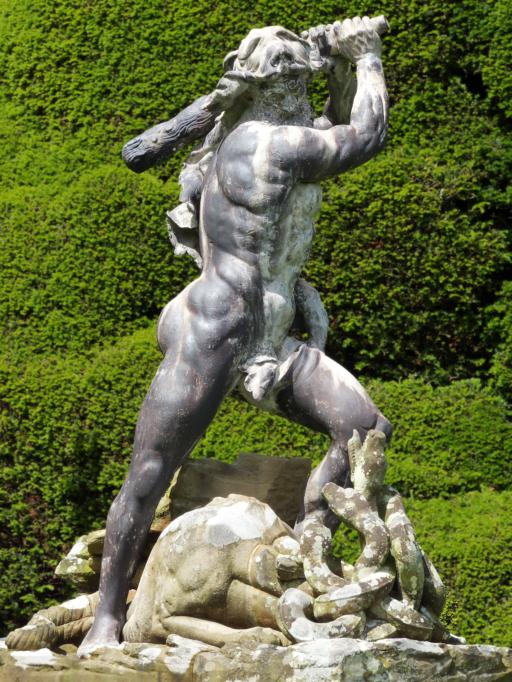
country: GB
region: Wales
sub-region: Sir Powys
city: Welshpool
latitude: 52.6503
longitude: -3.1596
